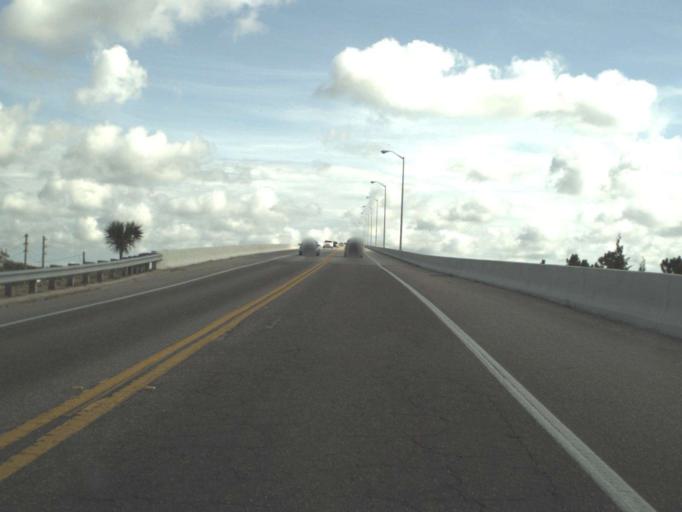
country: US
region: Florida
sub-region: Gulf County
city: Port Saint Joe
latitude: 29.8358
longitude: -85.3155
